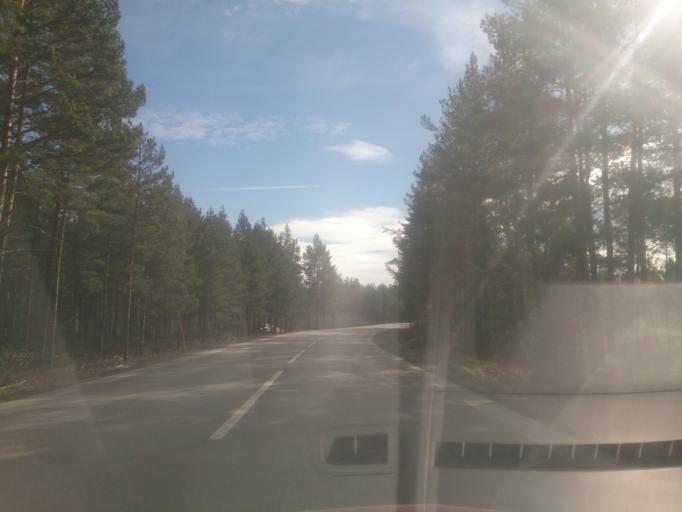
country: SE
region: OEstergoetland
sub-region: Finspangs Kommun
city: Finspang
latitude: 58.6631
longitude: 15.7787
